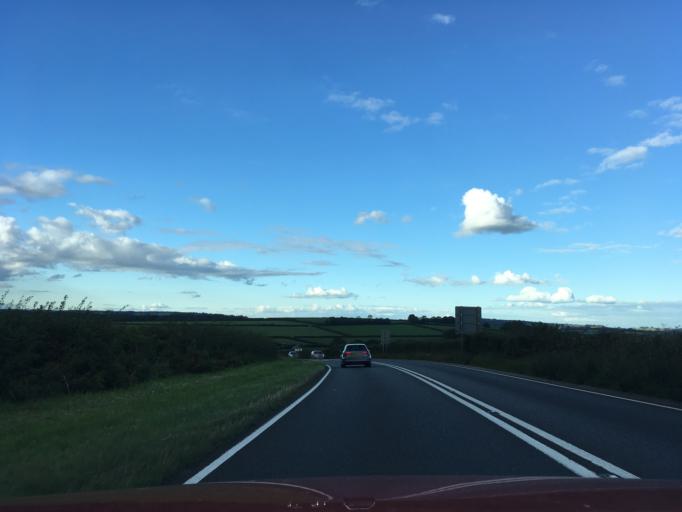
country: GB
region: England
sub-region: Somerset
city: Chard
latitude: 50.8842
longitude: -3.0841
